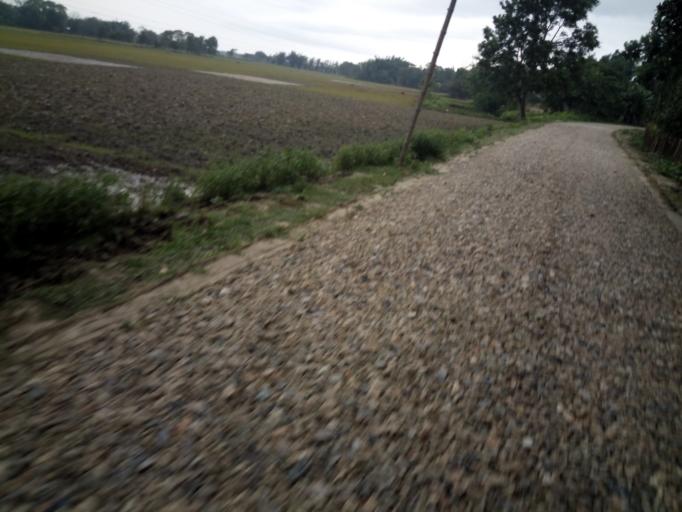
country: IN
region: Assam
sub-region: Darrang
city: Kharupatia
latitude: 26.6514
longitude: 92.2379
